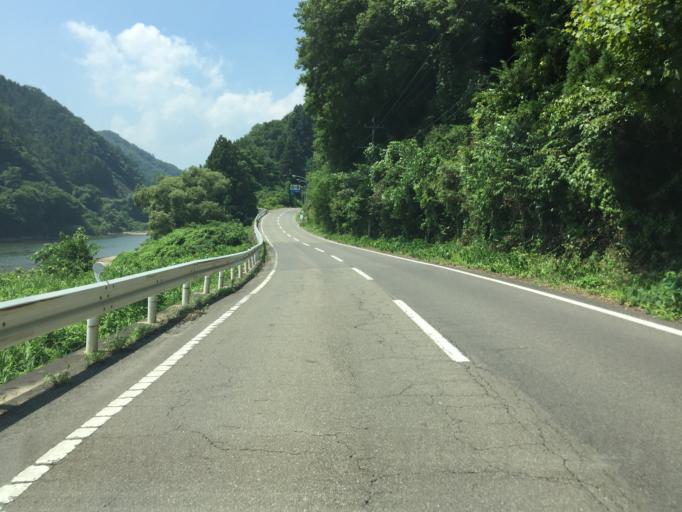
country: JP
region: Miyagi
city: Marumori
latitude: 37.9323
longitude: 140.7250
